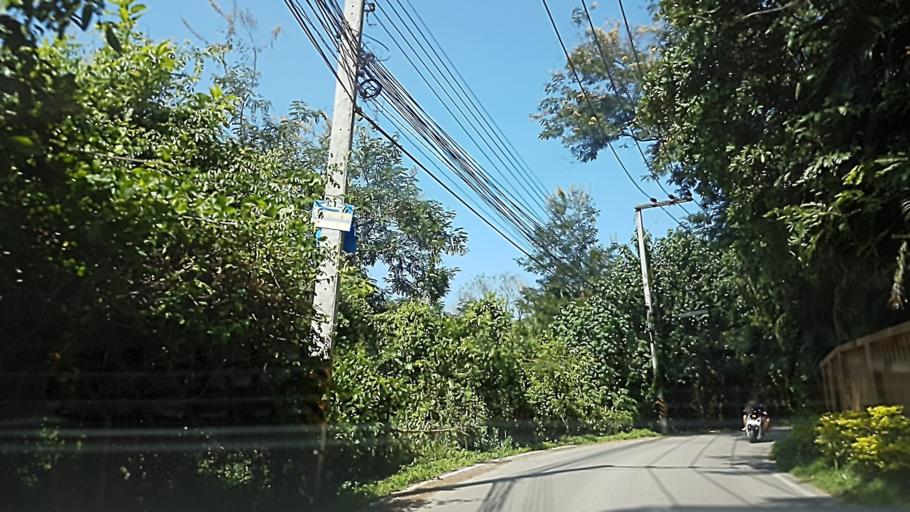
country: TH
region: Chiang Mai
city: Chiang Mai
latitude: 18.8222
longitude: 98.9567
